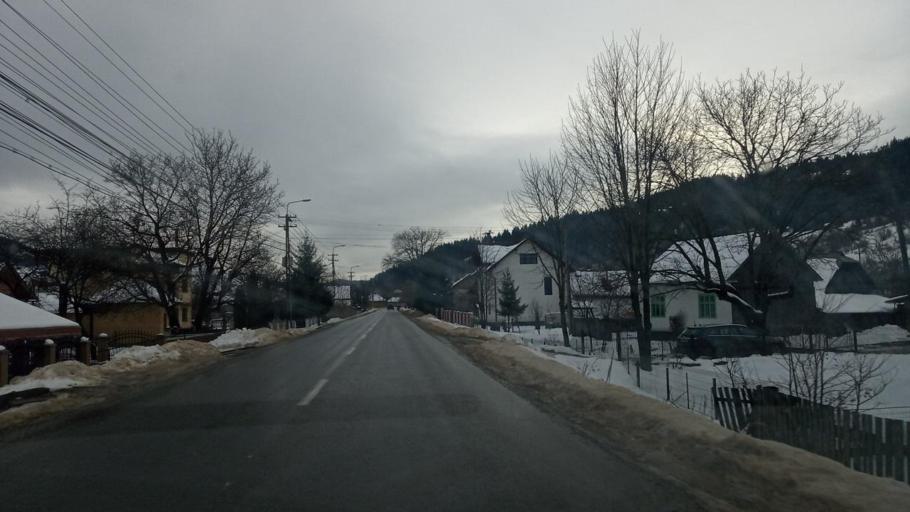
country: RO
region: Suceava
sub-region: Comuna Frasin
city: Frasin
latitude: 47.5244
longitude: 25.7980
